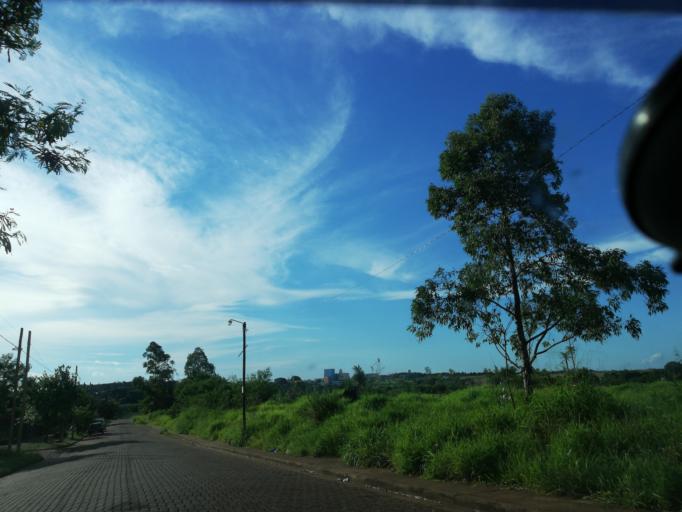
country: AR
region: Misiones
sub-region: Departamento de Capital
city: Posadas
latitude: -27.4041
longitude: -55.9530
